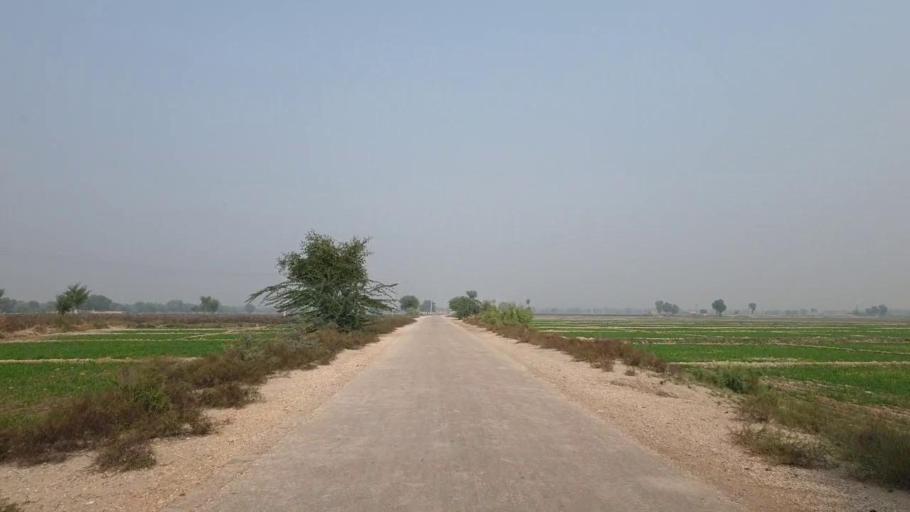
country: PK
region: Sindh
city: Bhan
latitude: 26.5257
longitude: 67.6928
